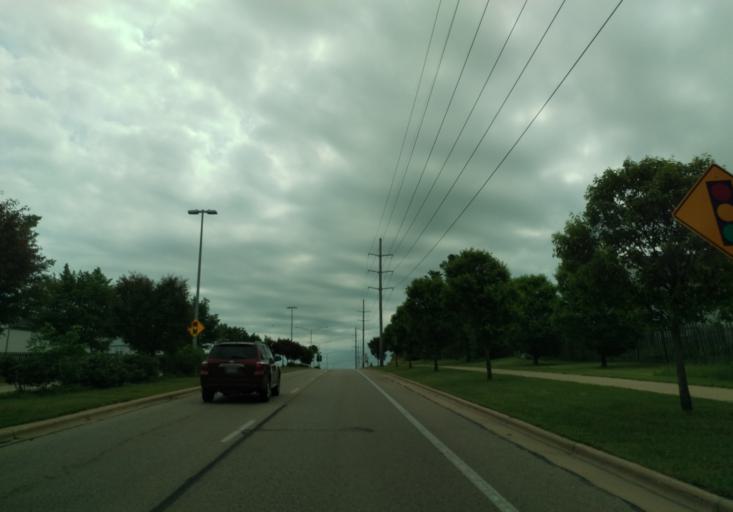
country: US
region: Wisconsin
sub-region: Dane County
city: Verona
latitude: 43.0157
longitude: -89.4859
